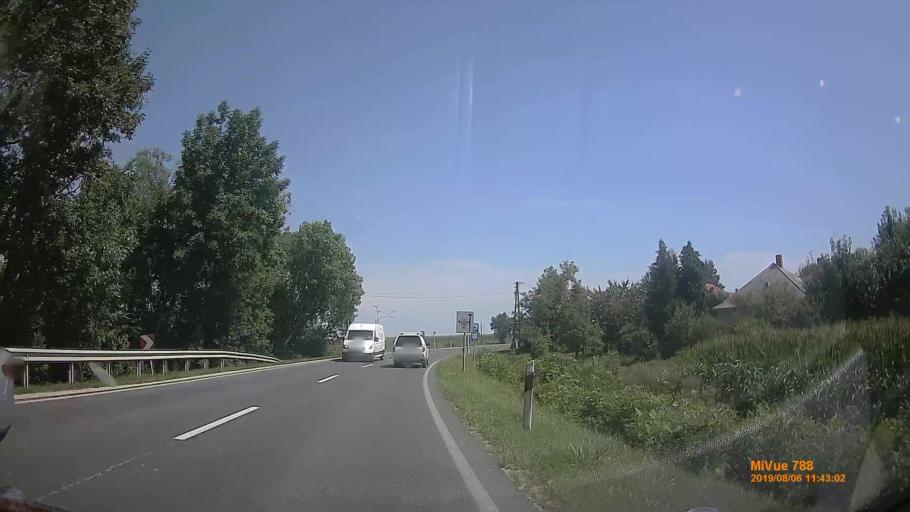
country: HU
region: Vas
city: Kormend
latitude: 47.0049
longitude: 16.5458
